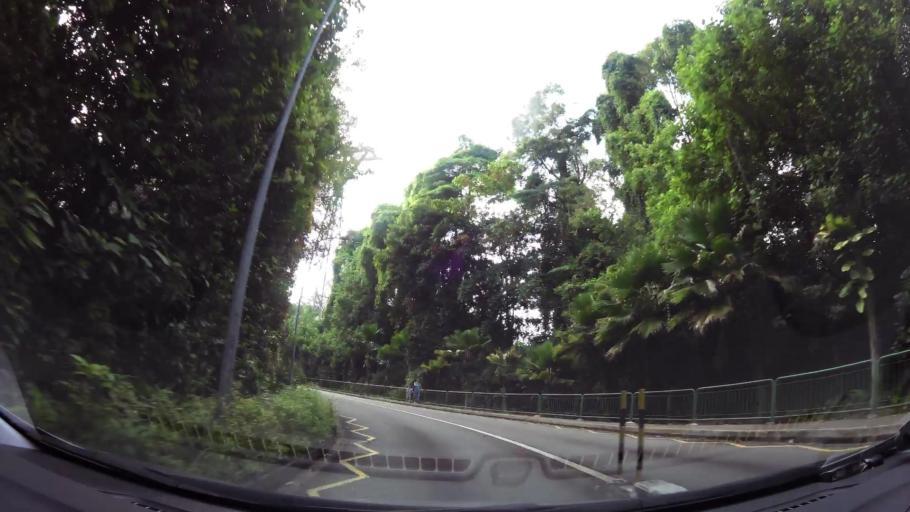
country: SG
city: Singapore
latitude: 1.2572
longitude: 103.8124
